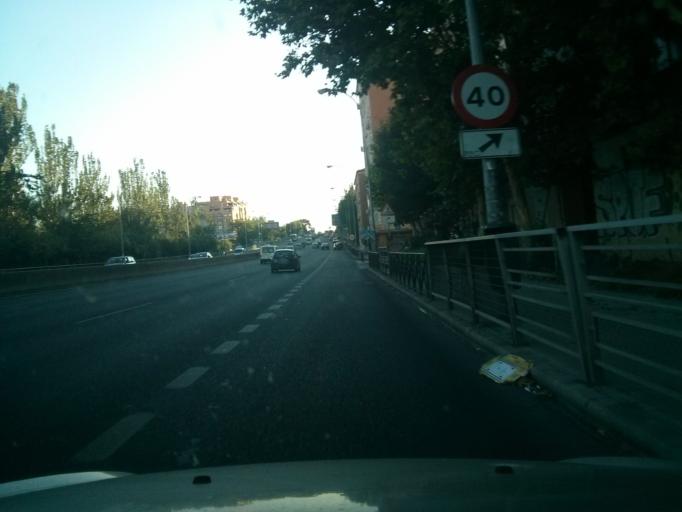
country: ES
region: Madrid
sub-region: Provincia de Madrid
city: Latina
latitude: 40.4046
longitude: -3.7536
